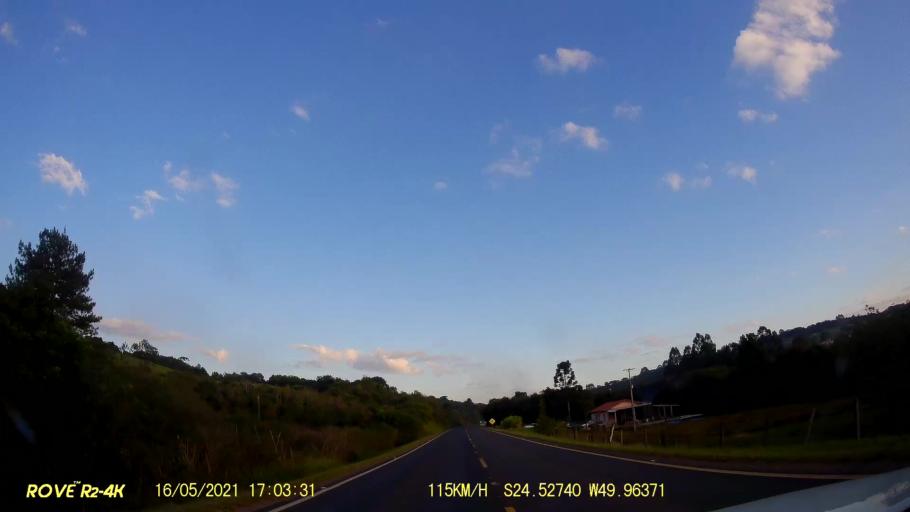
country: BR
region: Parana
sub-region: Pirai Do Sul
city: Pirai do Sul
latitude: -24.5275
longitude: -49.9637
